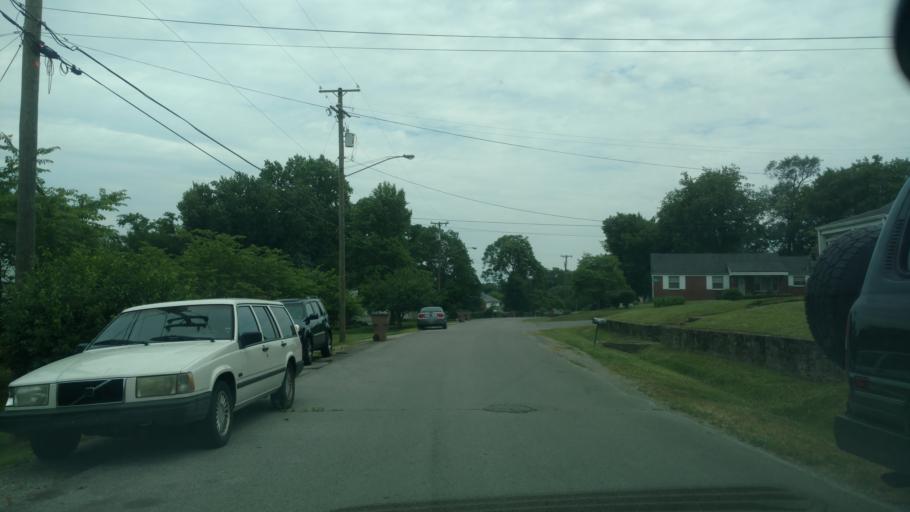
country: US
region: Tennessee
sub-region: Davidson County
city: Nashville
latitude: 36.1911
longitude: -86.7165
